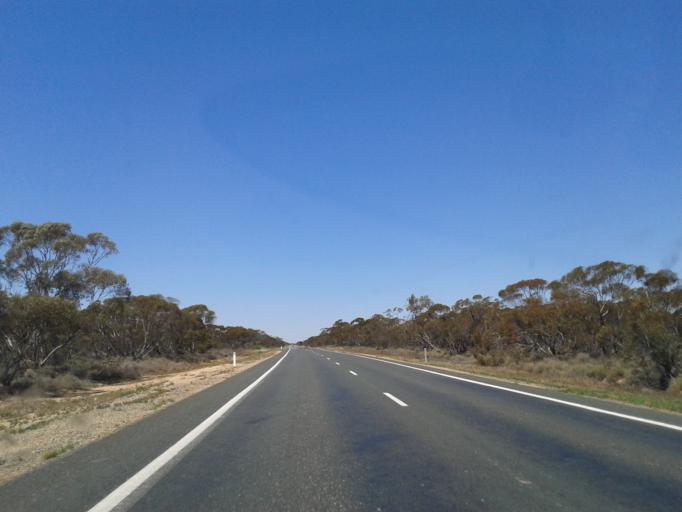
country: AU
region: New South Wales
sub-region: Wentworth
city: Gol Gol
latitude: -34.4315
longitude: 142.4598
